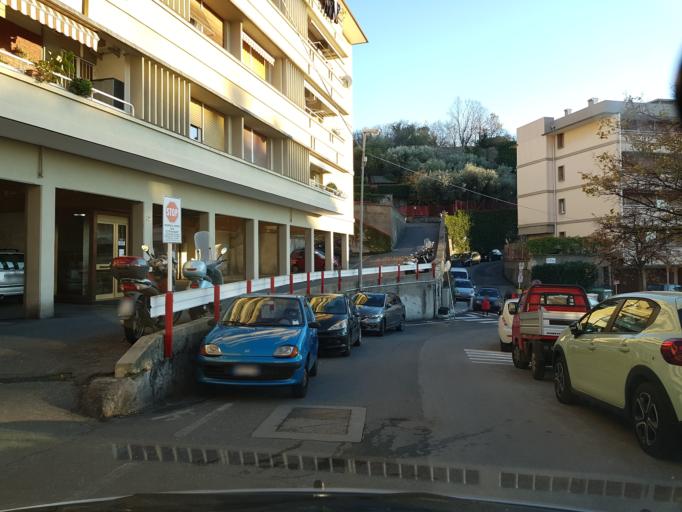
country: IT
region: Liguria
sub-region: Provincia di Genova
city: Genoa
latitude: 44.4082
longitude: 8.9825
